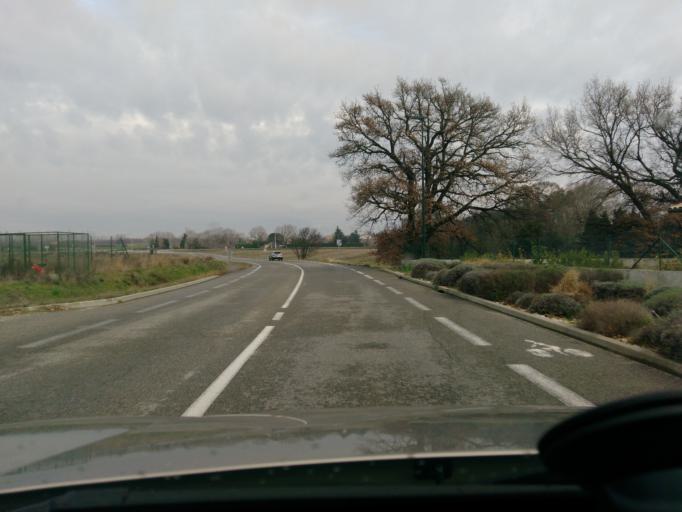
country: FR
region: Rhone-Alpes
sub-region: Departement de la Drome
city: Savasse
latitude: 44.5789
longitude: 4.7713
